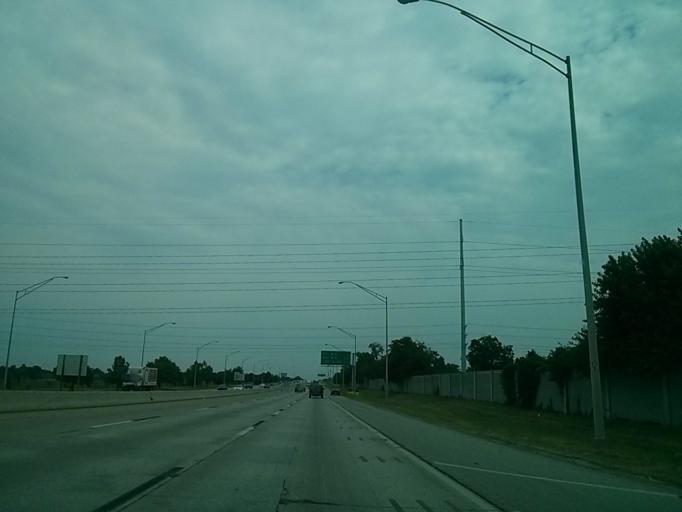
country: US
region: Oklahoma
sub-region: Tulsa County
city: Broken Arrow
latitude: 36.1107
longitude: -95.8595
